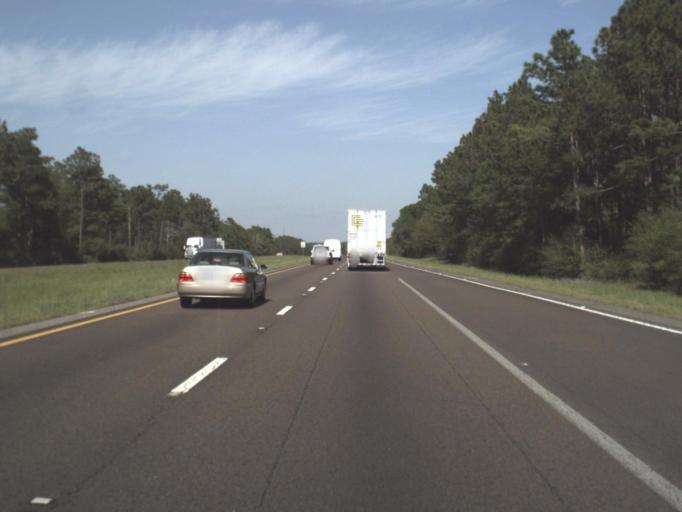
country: US
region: Florida
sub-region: Okaloosa County
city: Crestview
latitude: 30.7006
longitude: -86.7458
